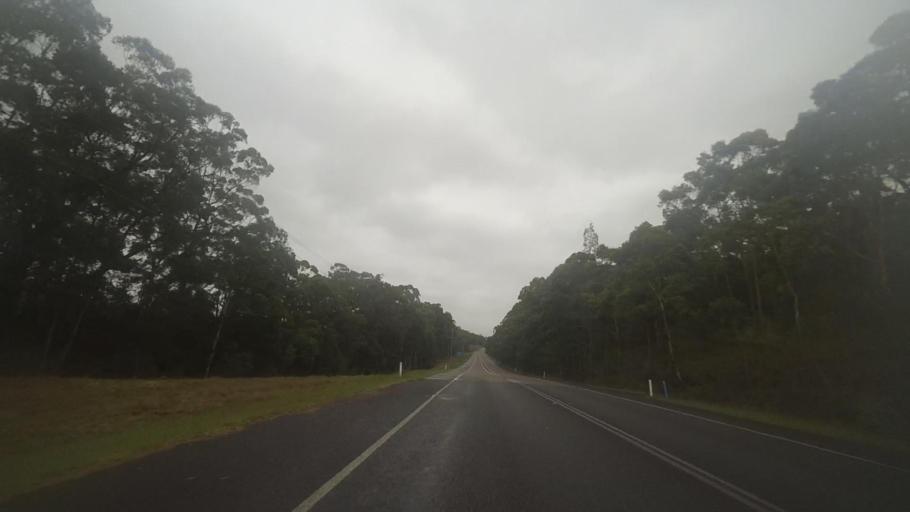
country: AU
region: New South Wales
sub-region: Port Stephens Shire
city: Port Stephens
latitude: -32.6400
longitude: 151.9916
